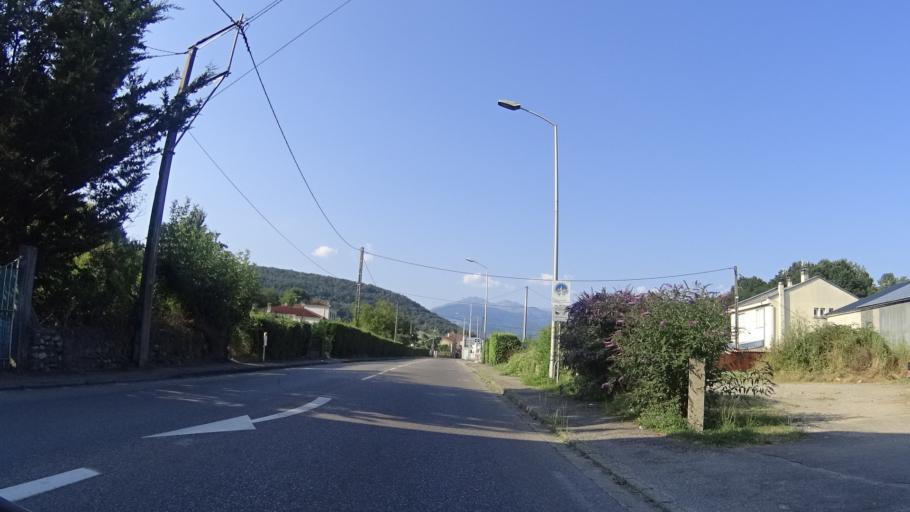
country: FR
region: Midi-Pyrenees
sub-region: Departement de l'Ariege
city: Lavelanet
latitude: 42.9447
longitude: 1.8576
